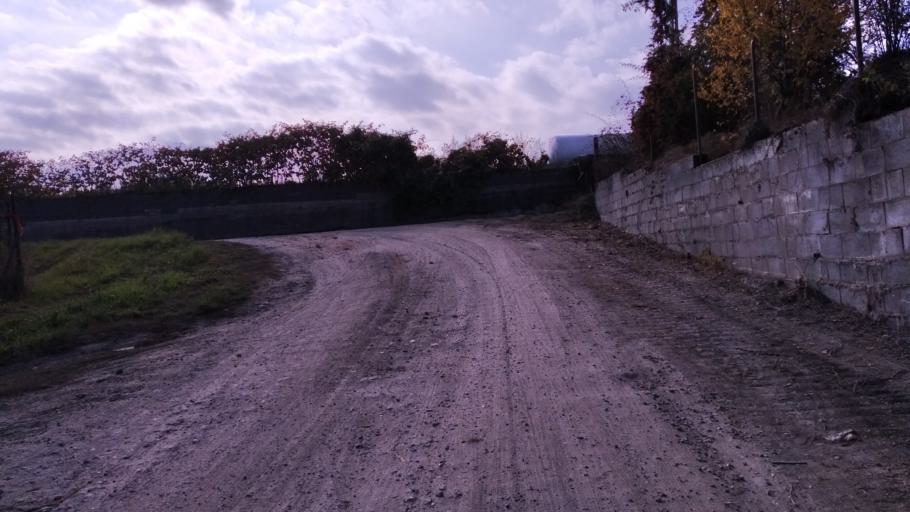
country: HU
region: Pest
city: Pomaz
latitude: 47.6427
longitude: 19.0409
